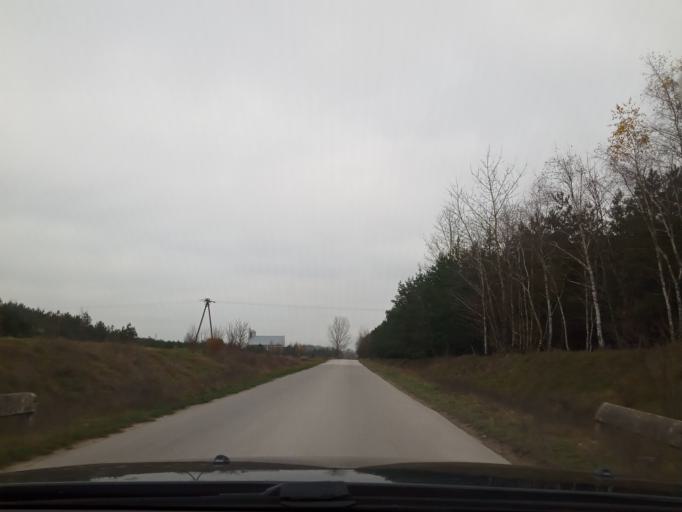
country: PL
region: Swietokrzyskie
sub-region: Powiat jedrzejowski
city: Imielno
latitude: 50.5975
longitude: 20.4833
